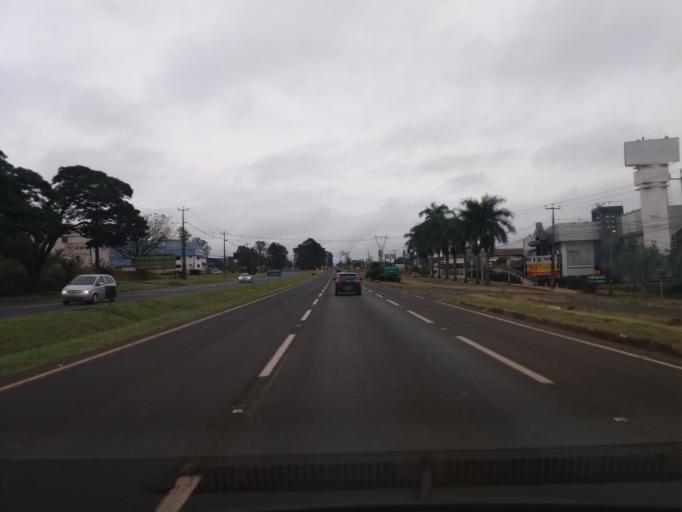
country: BR
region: Parana
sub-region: Paicandu
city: Paicandu
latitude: -23.4585
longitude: -51.9903
